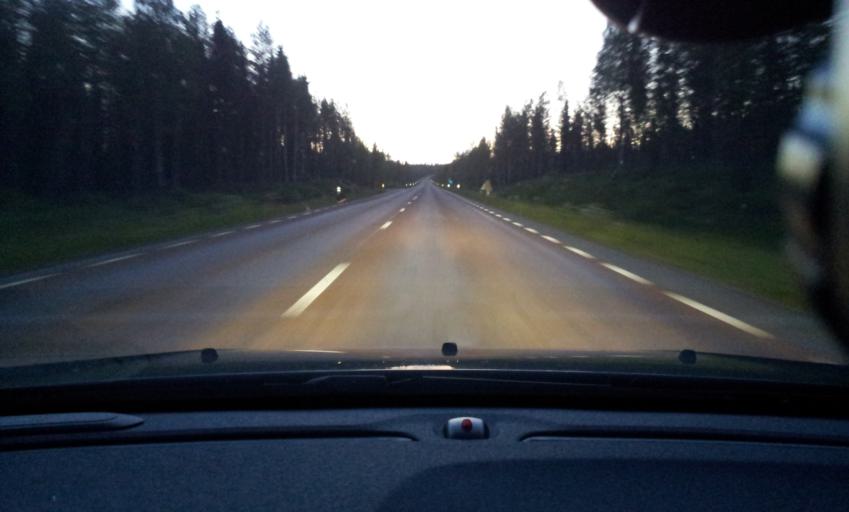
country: SE
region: Jaemtland
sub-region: Bergs Kommun
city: Hoverberg
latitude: 62.8110
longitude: 14.5179
